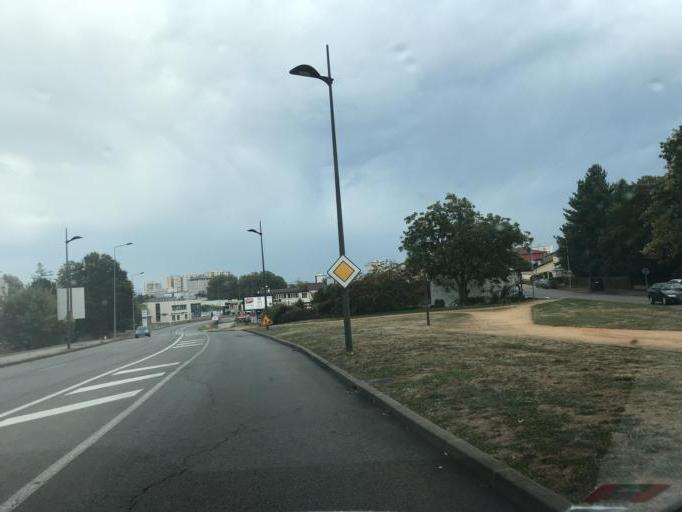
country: FR
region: Rhone-Alpes
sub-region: Departement de l'Ain
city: Bourg-en-Bresse
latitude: 46.2146
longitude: 5.2157
